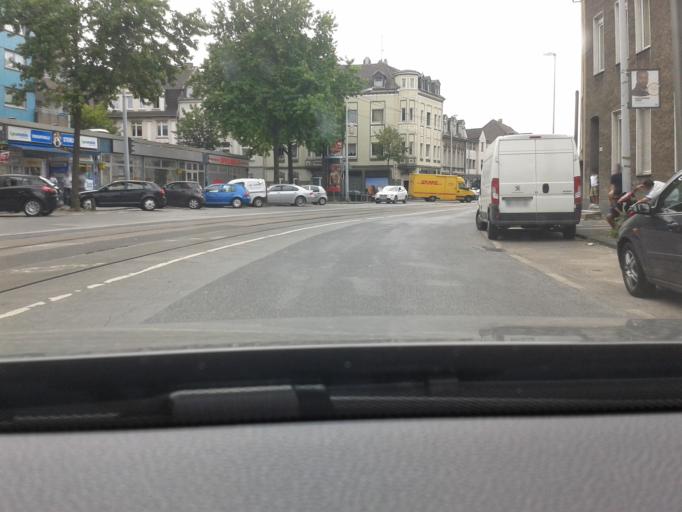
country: DE
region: North Rhine-Westphalia
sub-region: Regierungsbezirk Dusseldorf
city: Oberhausen
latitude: 51.4529
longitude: 6.8603
